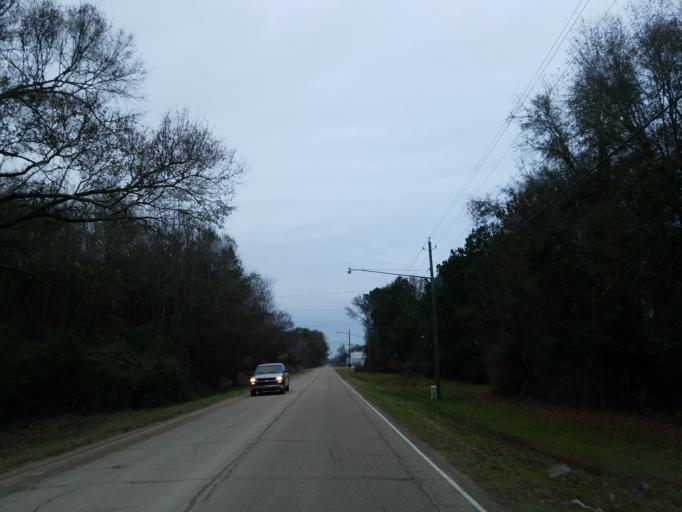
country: US
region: Mississippi
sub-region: Forrest County
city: Hattiesburg
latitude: 31.3015
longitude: -89.2762
